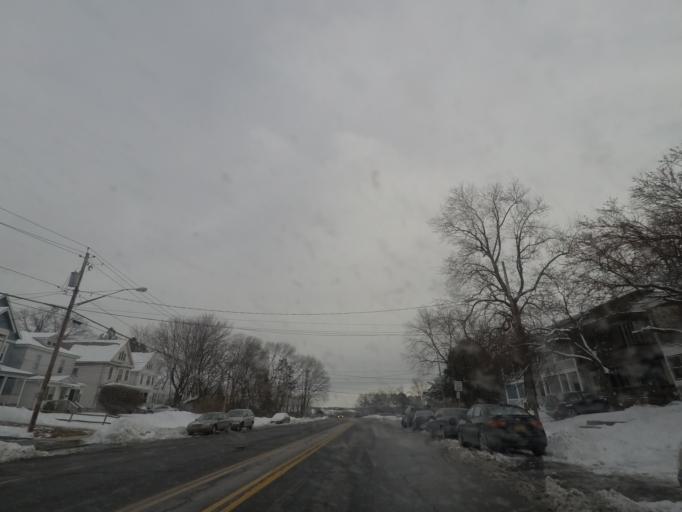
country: US
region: New York
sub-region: Albany County
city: Albany
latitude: 42.6667
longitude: -73.7570
